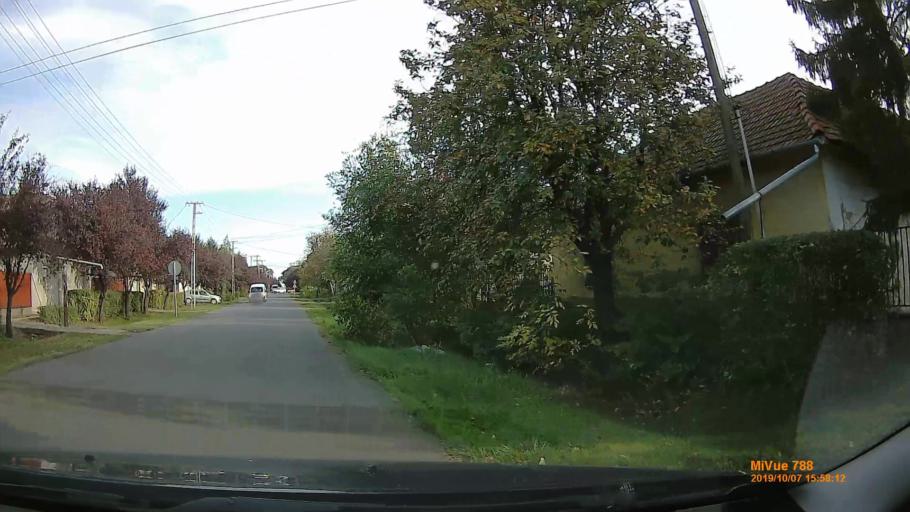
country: HU
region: Bekes
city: Szarvas
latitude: 46.8296
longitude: 20.6430
